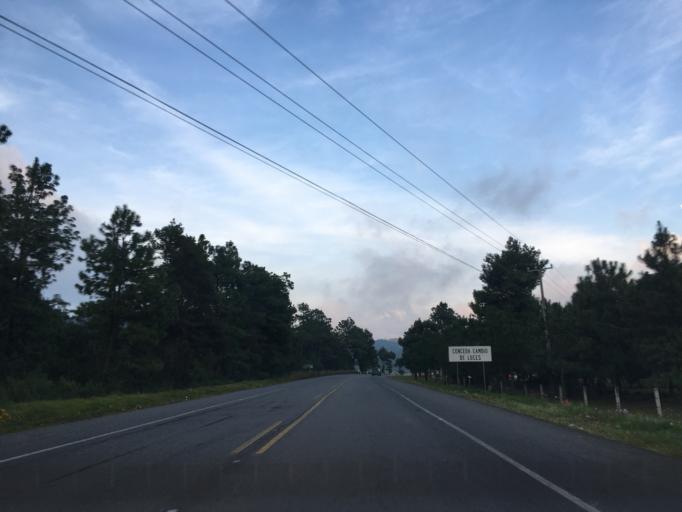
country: MX
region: Michoacan
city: Angahuan
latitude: 19.5714
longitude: -102.2638
